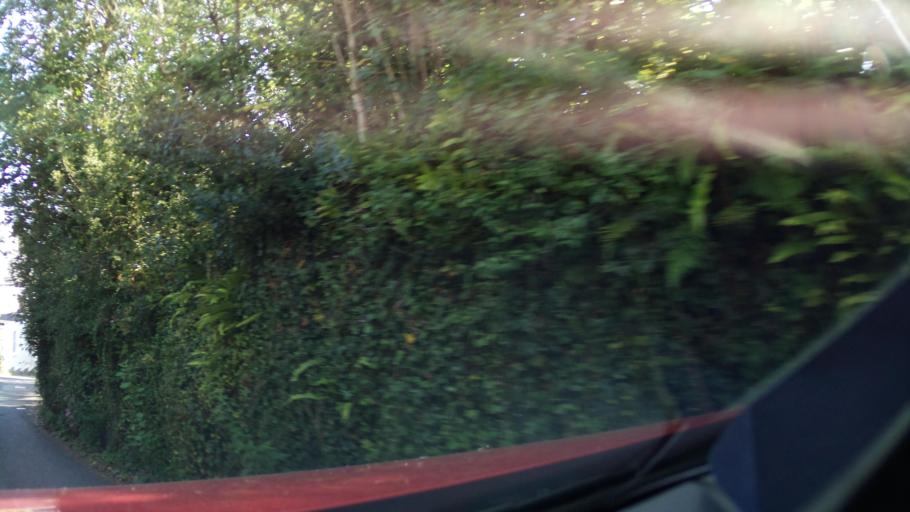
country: GB
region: England
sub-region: Devon
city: Totnes
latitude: 50.4146
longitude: -3.7225
